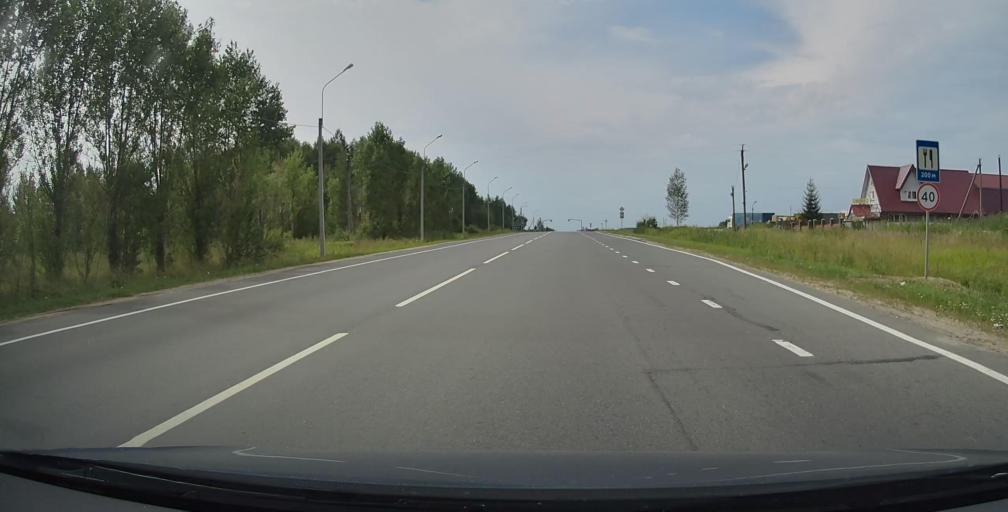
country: RU
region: Jaroslavl
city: Pesochnoye
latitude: 57.9862
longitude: 39.1189
